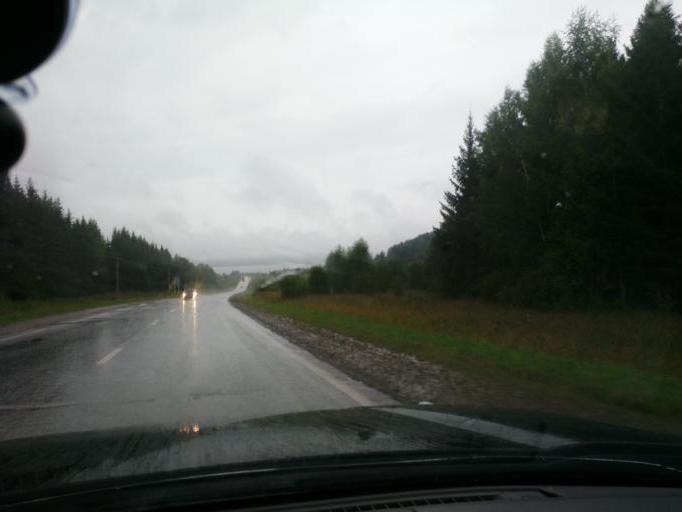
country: RU
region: Perm
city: Osa
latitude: 57.3259
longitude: 55.6016
